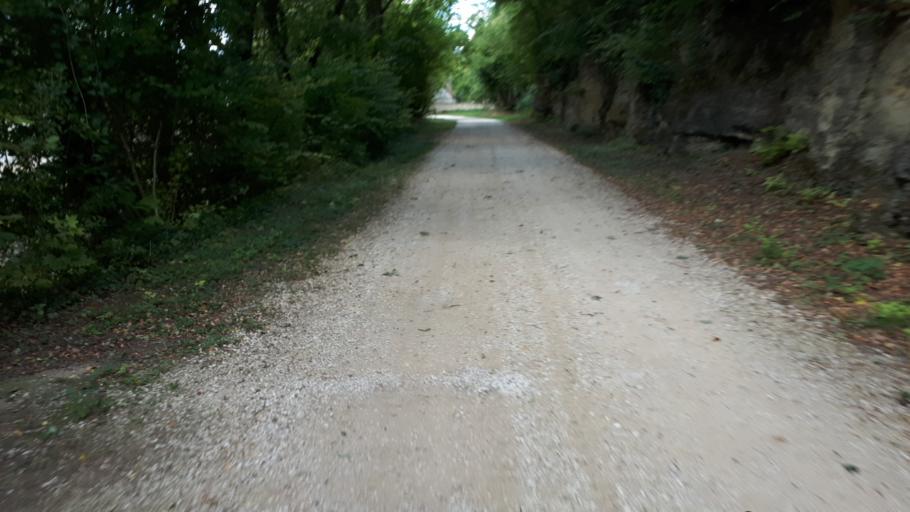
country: FR
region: Centre
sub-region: Departement du Loir-et-Cher
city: Villiers-sur-Loir
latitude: 47.7739
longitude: 0.9622
